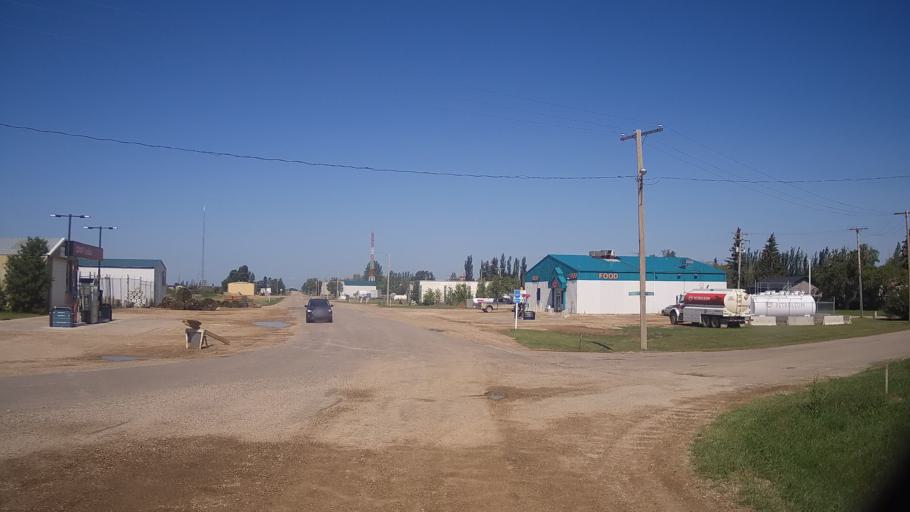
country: CA
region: Saskatchewan
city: Watrous
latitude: 51.8912
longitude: -106.0512
